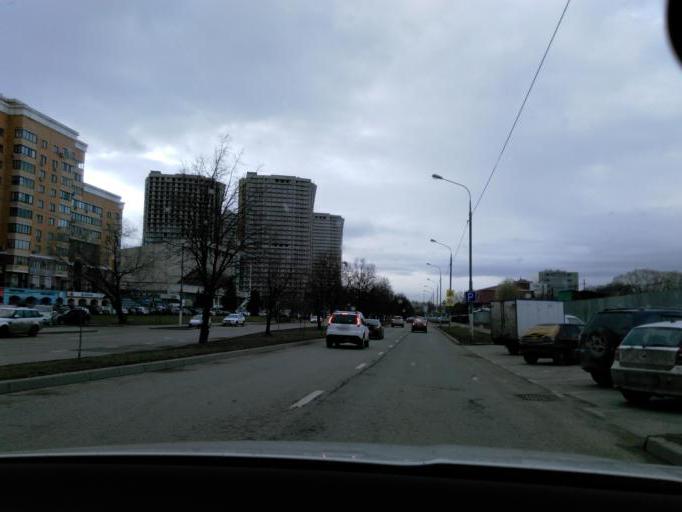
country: RU
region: Moscow
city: Golovinskiy
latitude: 55.8569
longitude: 37.4915
